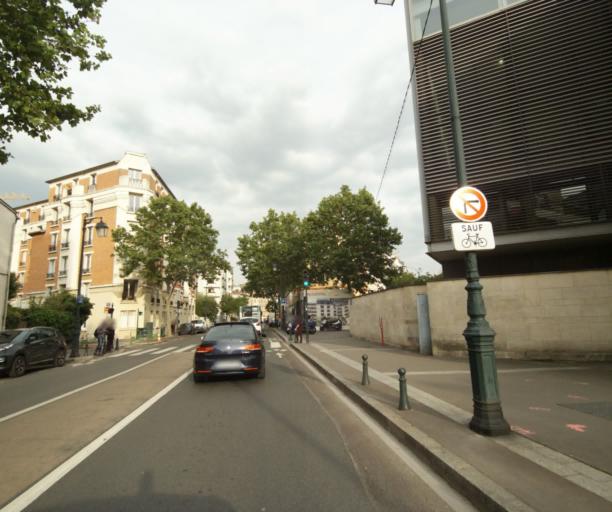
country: FR
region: Ile-de-France
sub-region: Paris
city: Saint-Ouen
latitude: 48.9017
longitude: 2.3241
